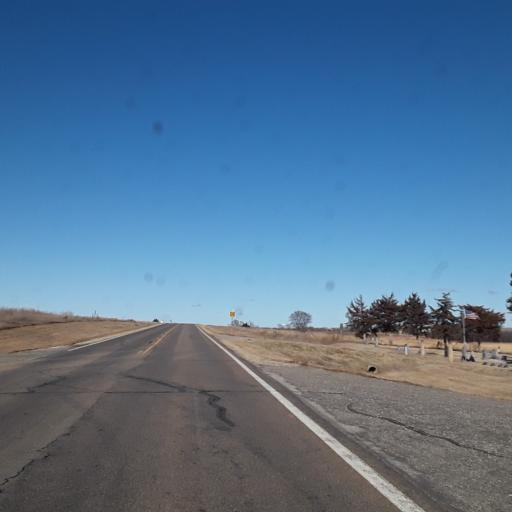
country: US
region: Kansas
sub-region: Lincoln County
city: Lincoln
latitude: 39.0153
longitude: -98.1516
